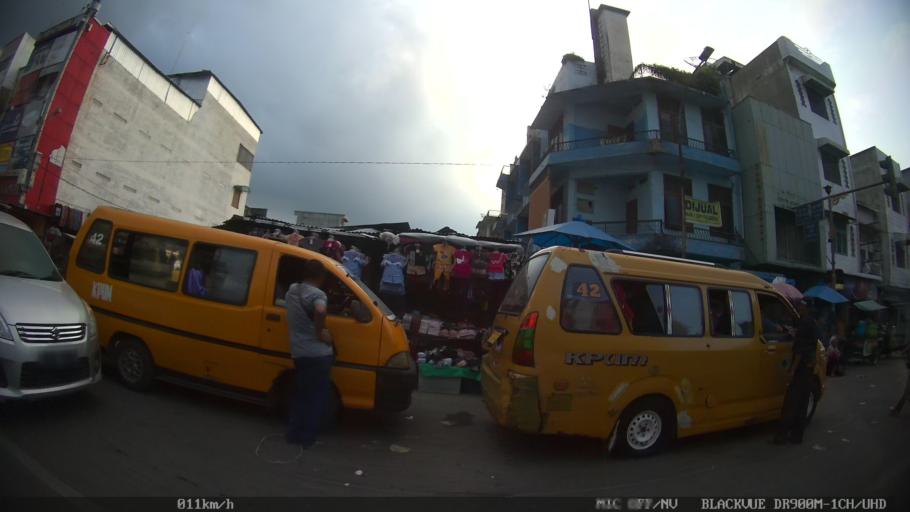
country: ID
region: North Sumatra
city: Medan
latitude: 3.5892
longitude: 98.6849
